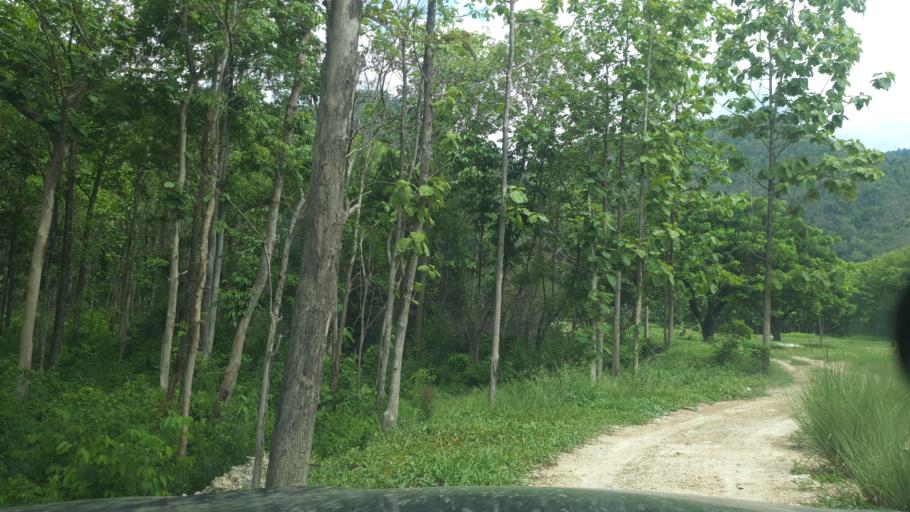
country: TH
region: Lampang
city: Sop Prap
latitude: 17.8545
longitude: 99.3973
